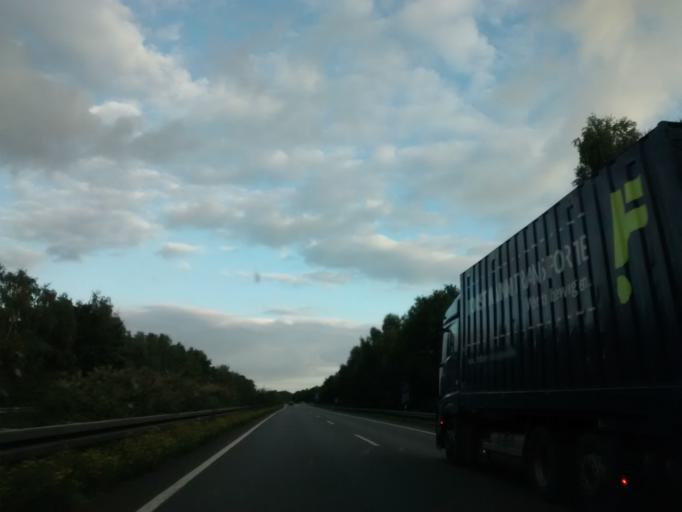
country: DE
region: North Rhine-Westphalia
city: Ibbenburen
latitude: 52.2599
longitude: 7.6987
